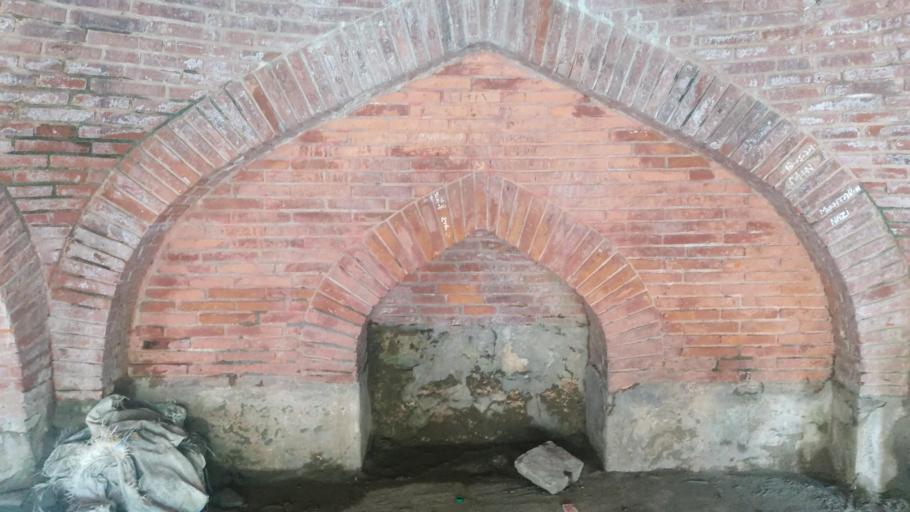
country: IN
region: Kashmir
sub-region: Ramban
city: Banihal
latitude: 33.5351
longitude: 75.2494
